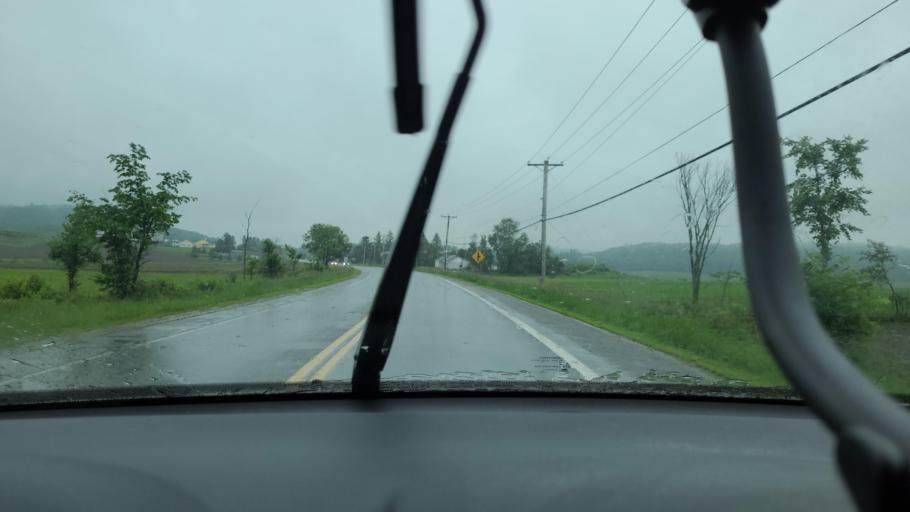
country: CA
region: Quebec
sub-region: Outaouais
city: Saint-Andre-Avellin
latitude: 45.6994
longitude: -75.0515
